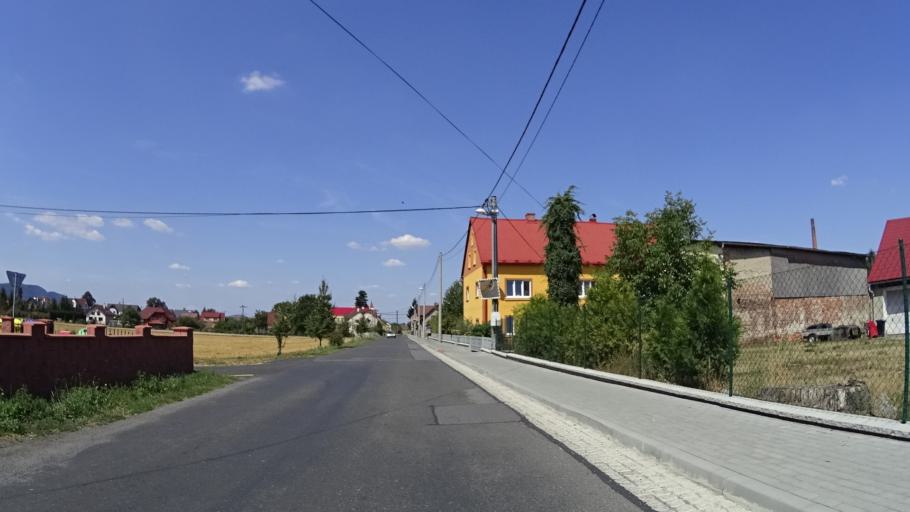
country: CZ
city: Hradek nad Nisou
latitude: 50.8451
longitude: 14.8551
